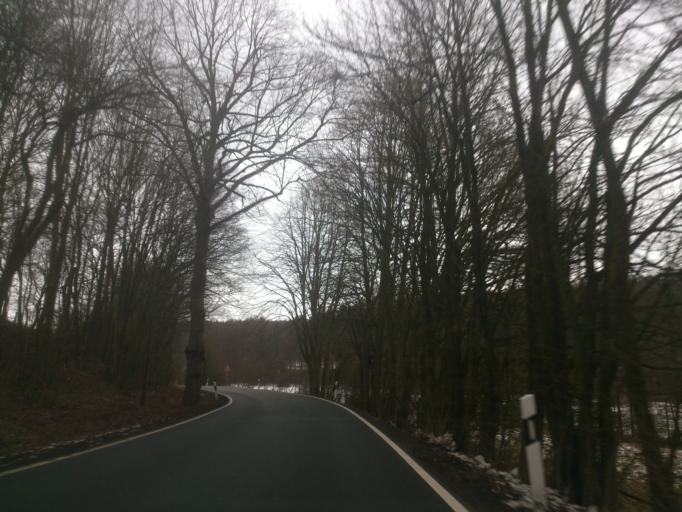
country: DE
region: North Rhine-Westphalia
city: Lichtenau
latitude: 51.6906
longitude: 8.8627
